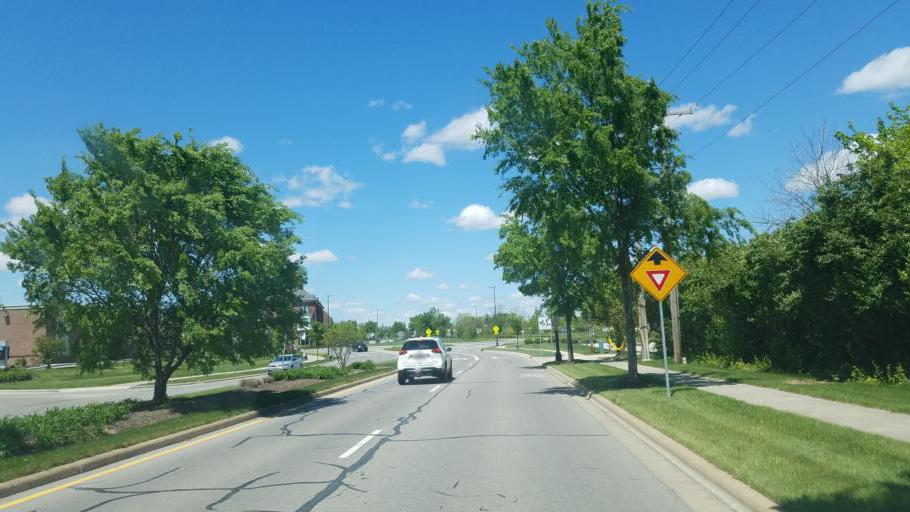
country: US
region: Ohio
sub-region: Franklin County
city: Hilliard
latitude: 40.0352
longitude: -83.1312
